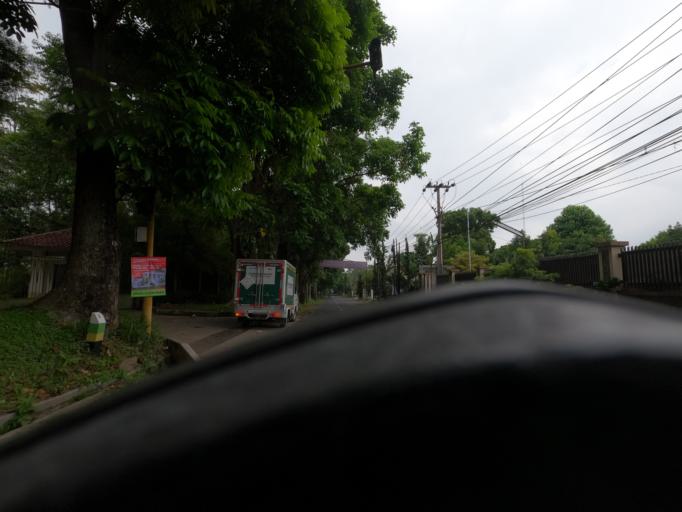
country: ID
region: West Java
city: Lembang
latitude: -6.7997
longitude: 107.5723
